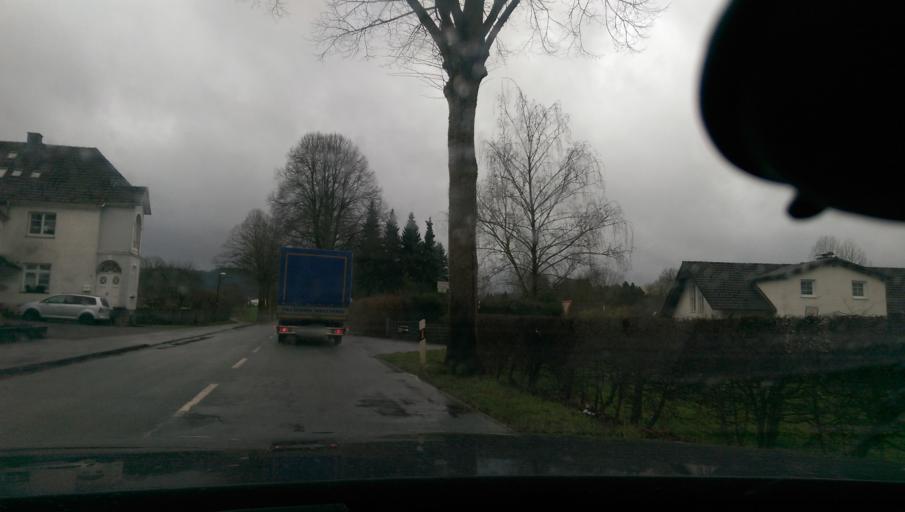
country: DE
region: North Rhine-Westphalia
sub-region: Regierungsbezirk Arnsberg
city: Sundern
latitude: 51.3040
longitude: 7.9877
